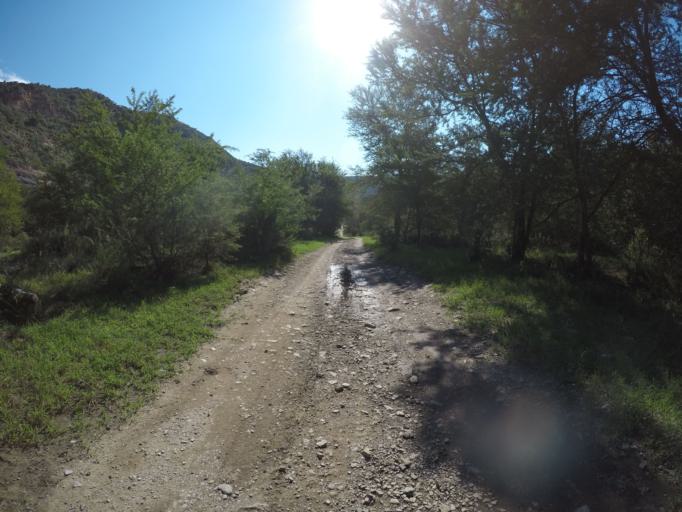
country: ZA
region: Eastern Cape
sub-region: Cacadu District Municipality
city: Kareedouw
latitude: -33.6608
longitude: 24.3671
